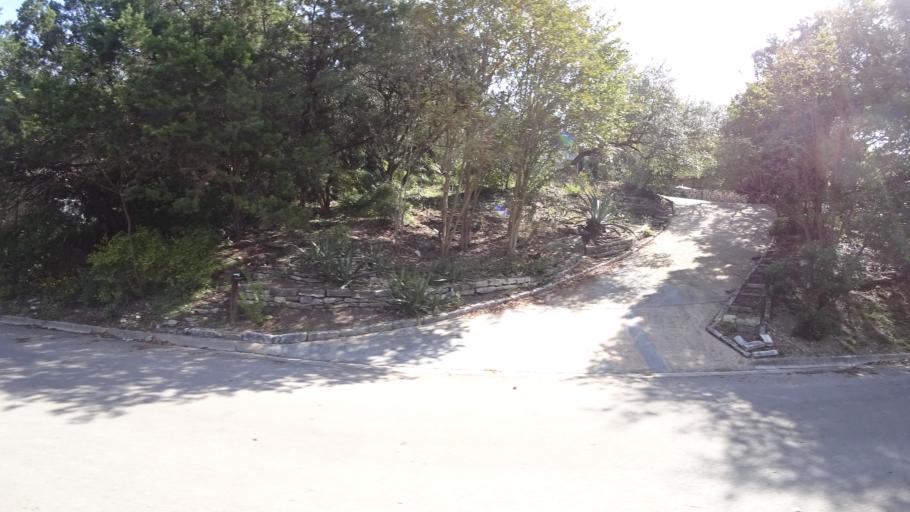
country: US
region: Texas
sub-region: Travis County
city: West Lake Hills
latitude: 30.3437
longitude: -97.7617
